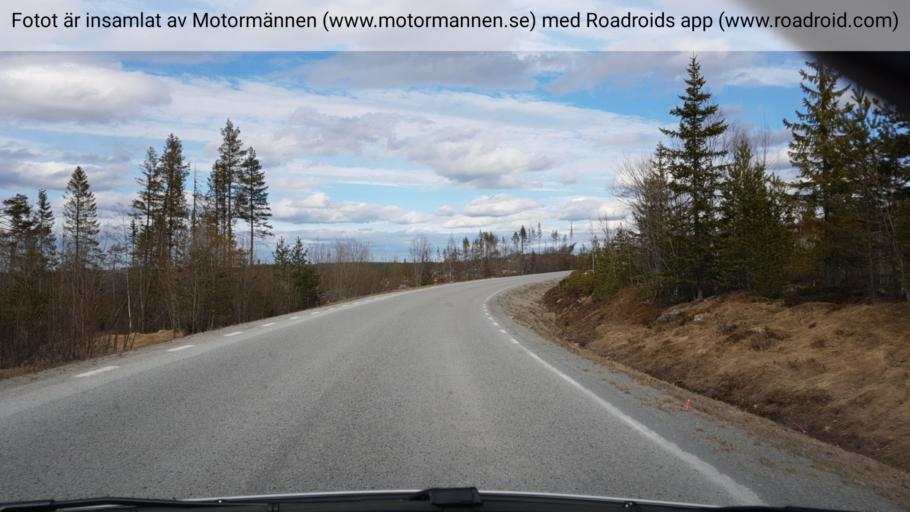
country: SE
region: Jaemtland
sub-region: Bergs Kommun
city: Hoverberg
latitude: 62.6767
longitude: 14.6917
